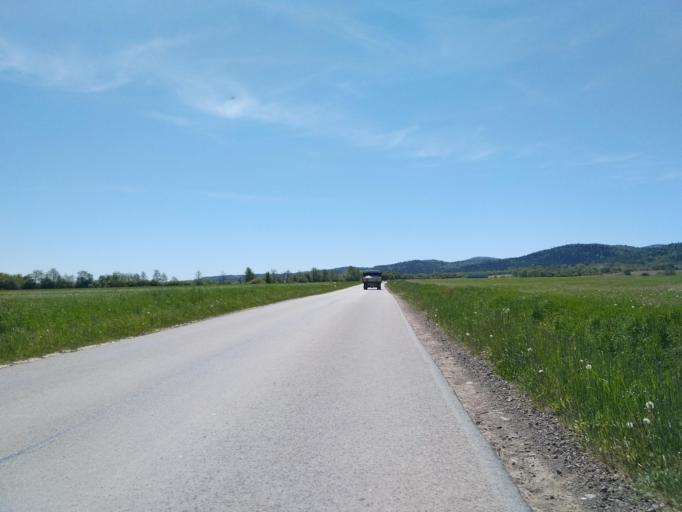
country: PL
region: Subcarpathian Voivodeship
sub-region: Powiat krosnienski
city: Sieniawa
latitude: 49.5362
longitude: 21.9719
